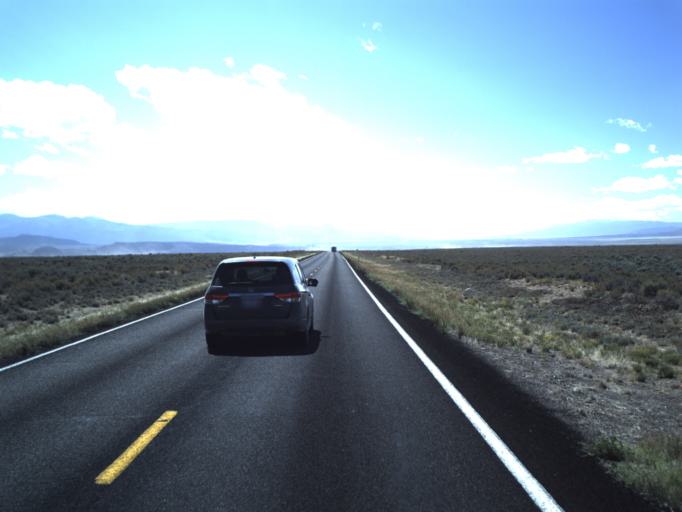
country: US
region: Utah
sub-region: Iron County
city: Enoch
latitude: 37.9967
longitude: -112.9993
